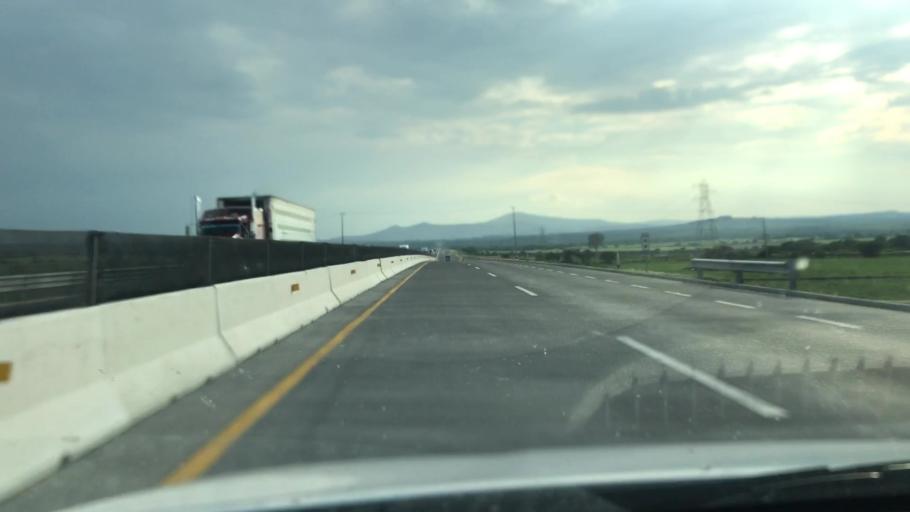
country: MX
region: Michoacan
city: La Piedad Cavadas
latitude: 20.3986
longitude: -102.0588
